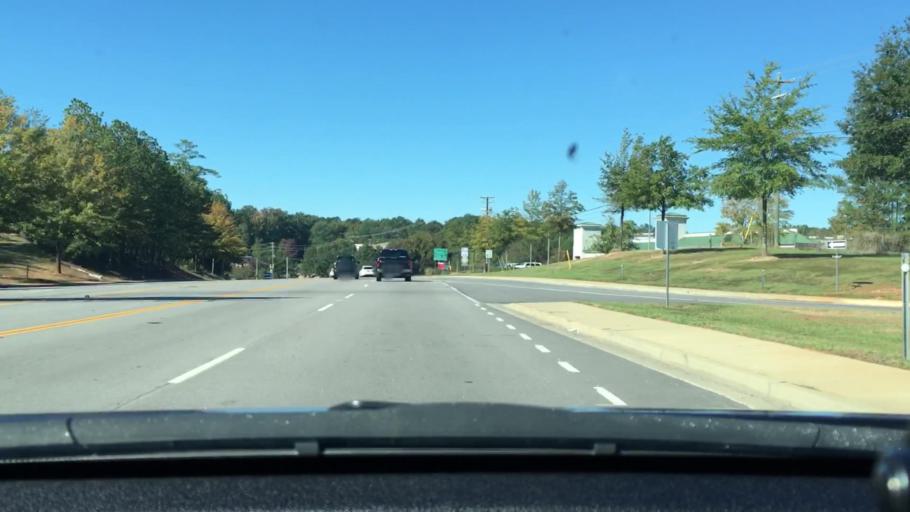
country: US
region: South Carolina
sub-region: Lexington County
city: Irmo
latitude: 34.0911
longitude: -81.1680
